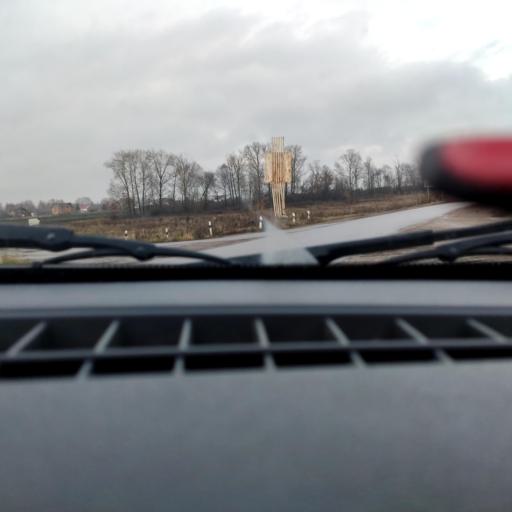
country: RU
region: Bashkortostan
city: Avdon
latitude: 54.5118
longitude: 55.8202
